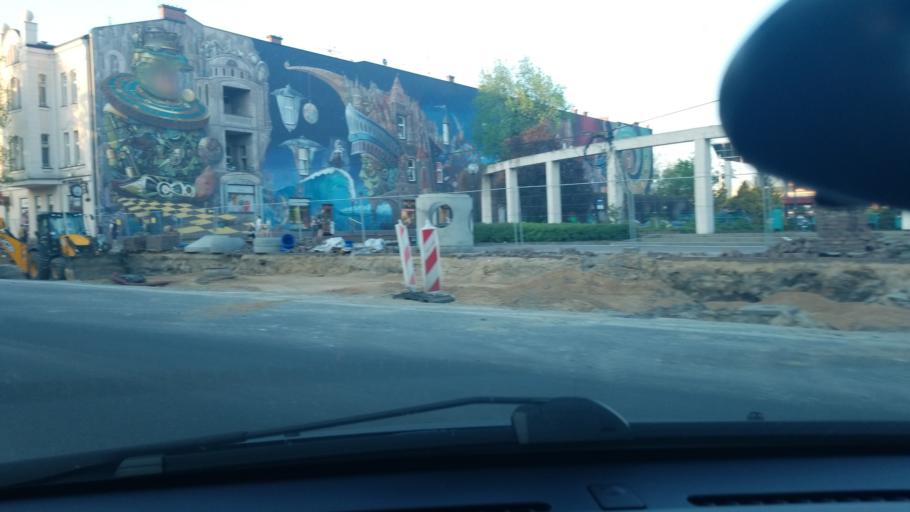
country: PL
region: Silesian Voivodeship
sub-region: Czestochowa
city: Czestochowa
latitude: 50.8087
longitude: 19.1181
